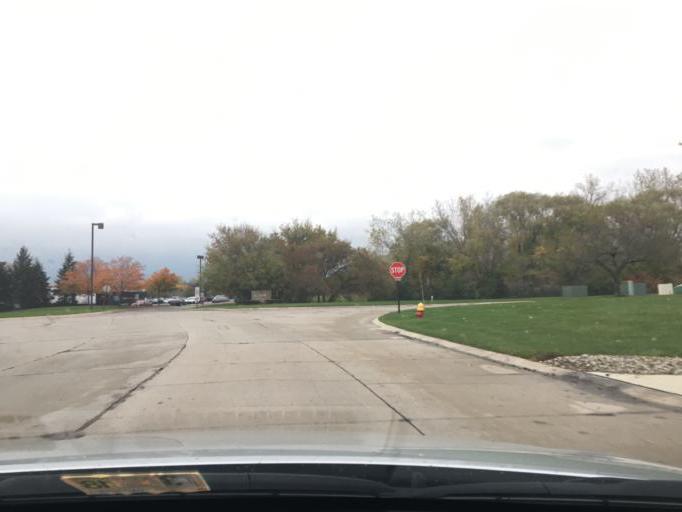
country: US
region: Michigan
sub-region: Wayne County
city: Melvindale
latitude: 42.2952
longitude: -83.1958
